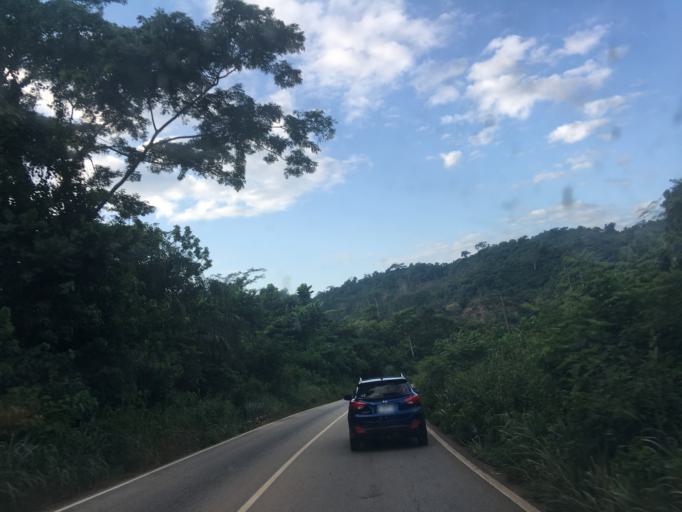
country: GH
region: Western
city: Bibiani
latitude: 6.4767
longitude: -2.3330
